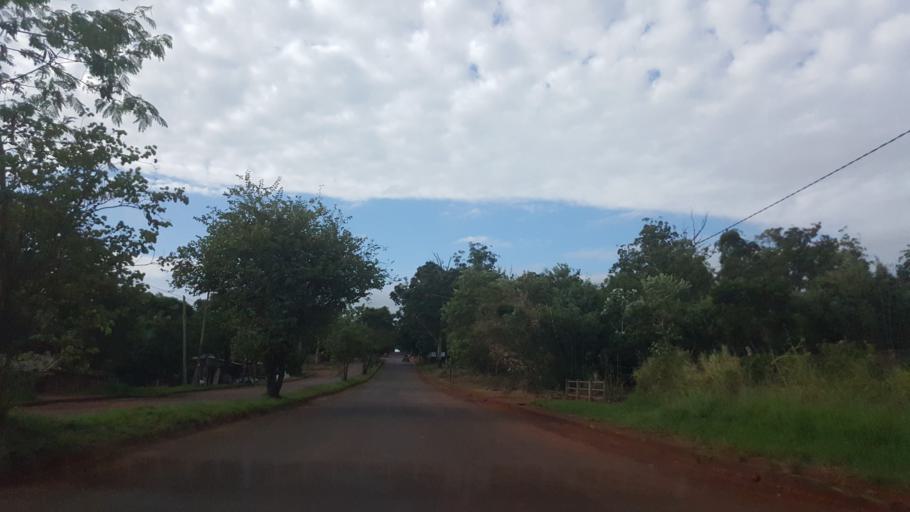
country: AR
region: Misiones
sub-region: Departamento de Capital
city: Posadas
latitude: -27.3927
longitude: -55.9352
